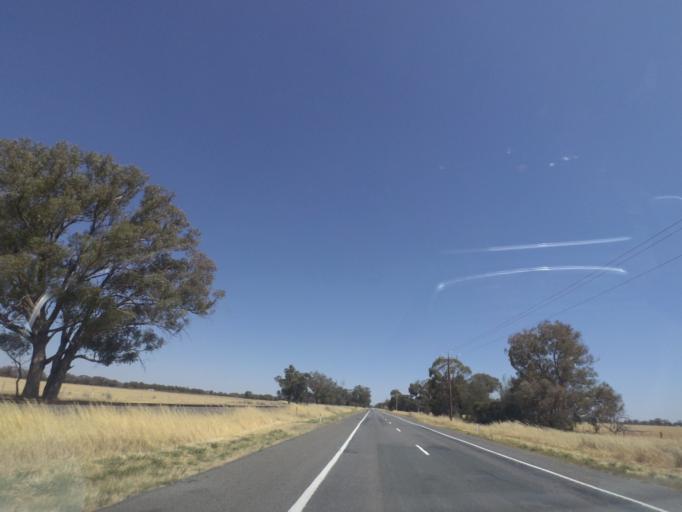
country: AU
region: Victoria
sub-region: Greater Shepparton
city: Shepparton
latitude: -36.2045
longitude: 145.4319
